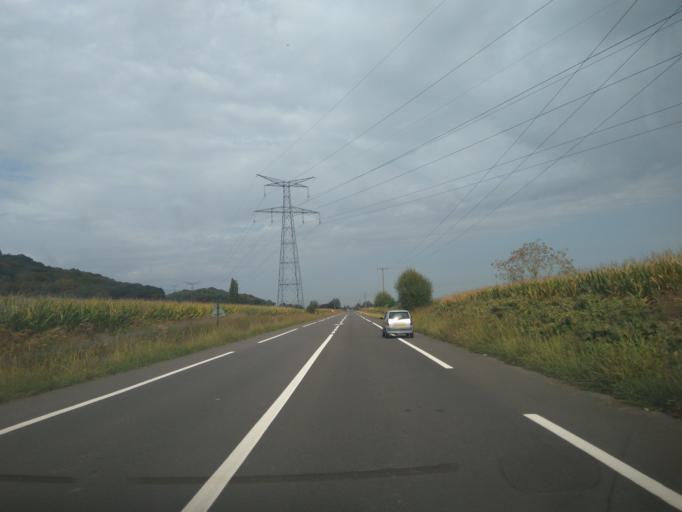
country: FR
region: Aquitaine
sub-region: Departement des Pyrenees-Atlantiques
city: Arbus
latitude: 43.3406
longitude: -0.5111
